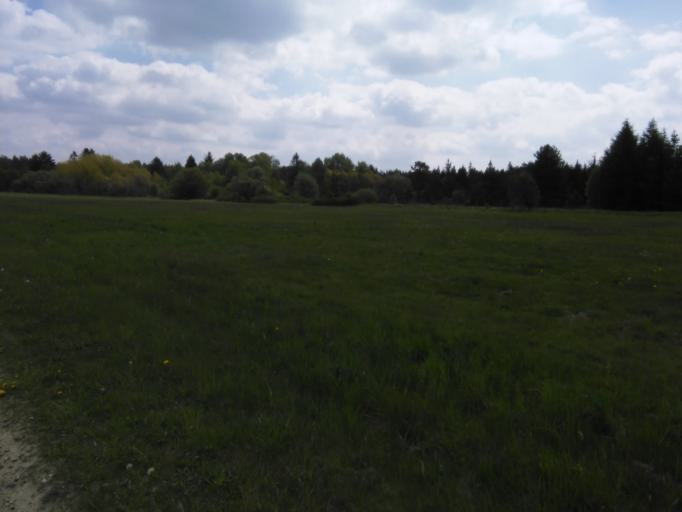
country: DK
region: Central Jutland
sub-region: Silkeborg Kommune
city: Svejbaek
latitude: 56.0524
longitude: 9.6721
